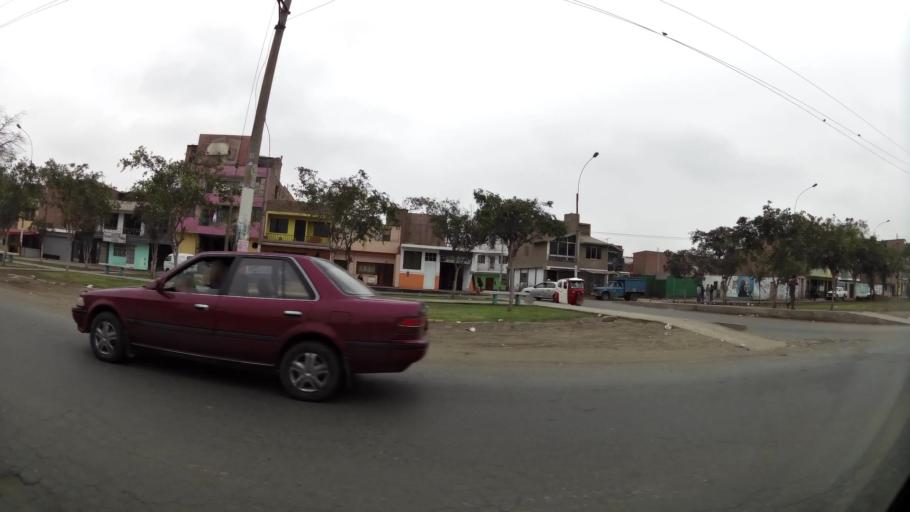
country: PE
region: Lima
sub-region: Lima
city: Independencia
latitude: -11.9435
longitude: -77.0667
